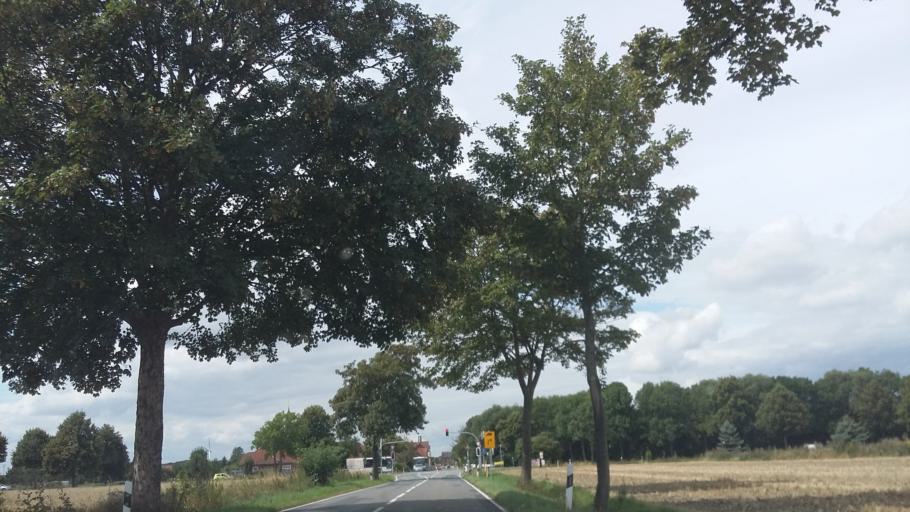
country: DE
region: Lower Saxony
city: Harsum
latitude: 52.2071
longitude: 9.9747
